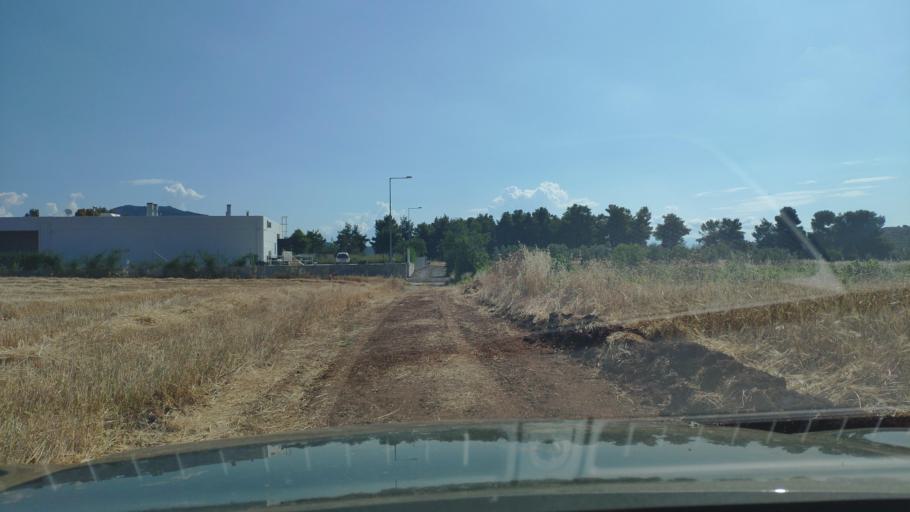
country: GR
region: Central Greece
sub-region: Nomos Voiotias
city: Arma
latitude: 38.3946
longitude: 23.5079
